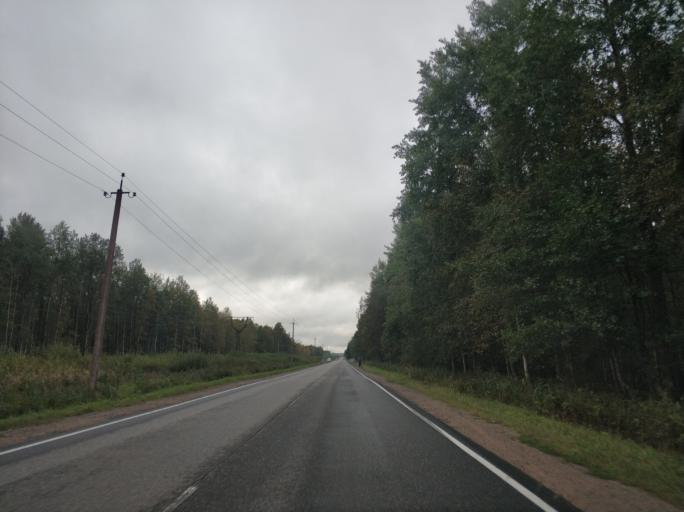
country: RU
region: Leningrad
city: Borisova Griva
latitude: 60.1102
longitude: 30.9611
